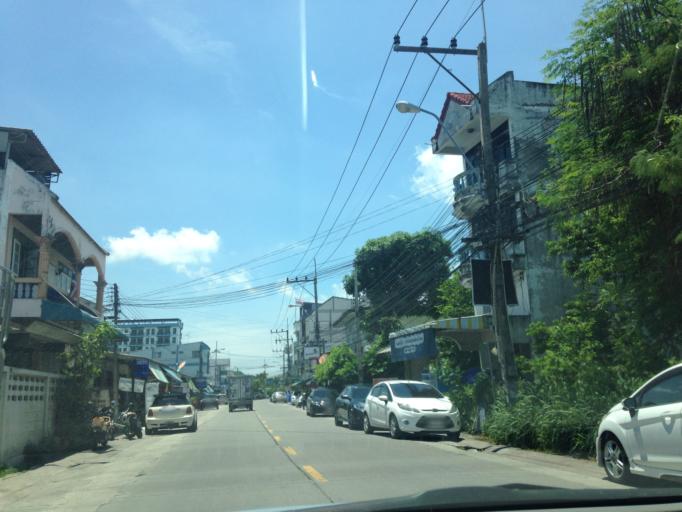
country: TH
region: Chon Buri
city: Chon Buri
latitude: 13.2878
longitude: 100.9371
